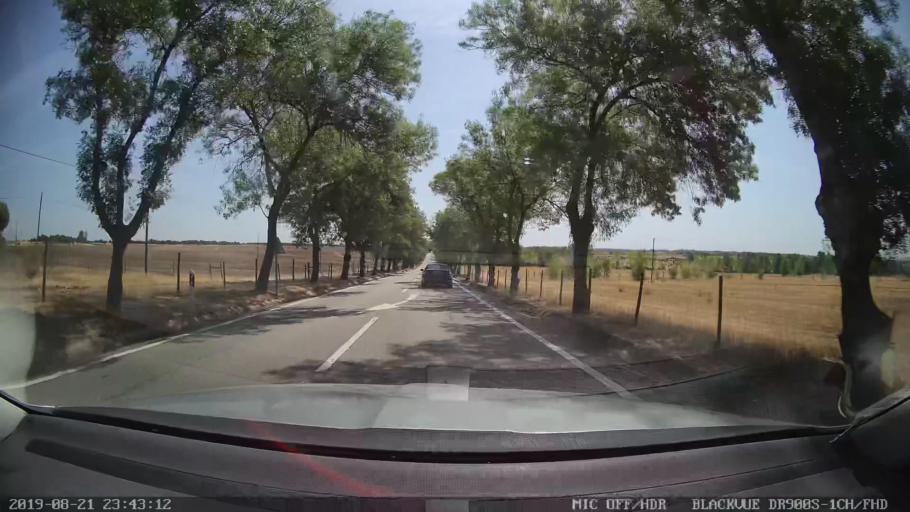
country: PT
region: Castelo Branco
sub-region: Idanha-A-Nova
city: Idanha-a-Nova
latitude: 39.8511
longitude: -7.2996
